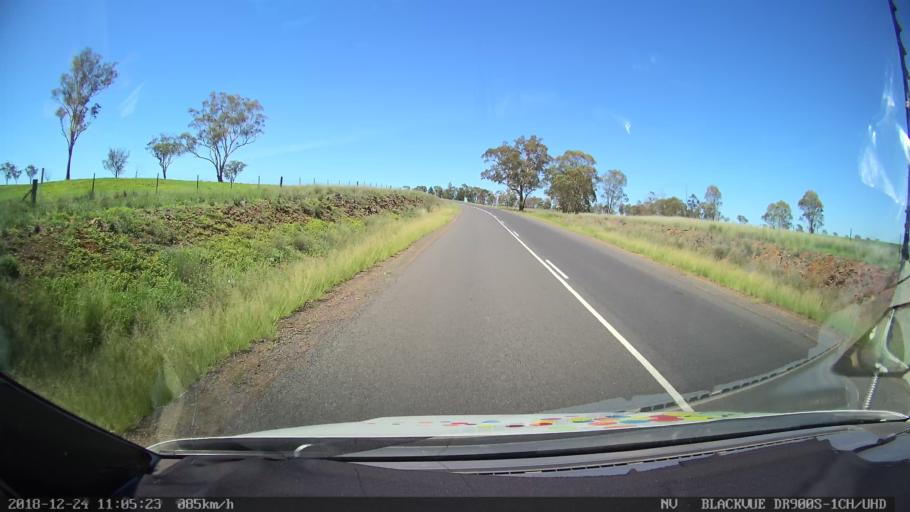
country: AU
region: New South Wales
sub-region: Upper Hunter Shire
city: Merriwa
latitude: -32.1202
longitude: 150.3714
